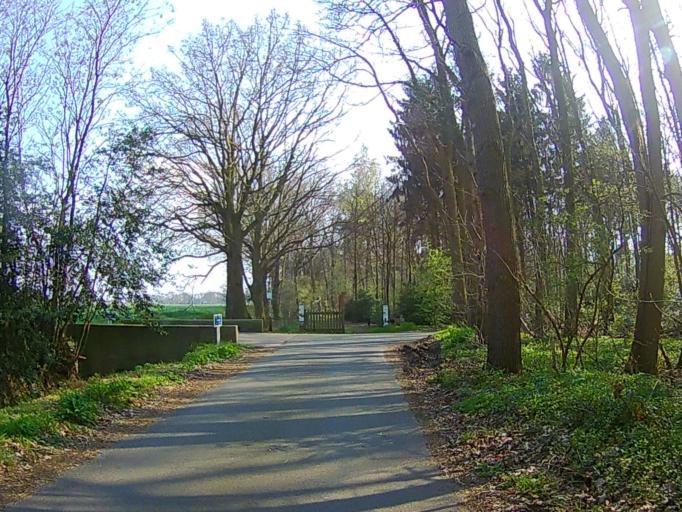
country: BE
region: Flanders
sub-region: Provincie Antwerpen
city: Essen
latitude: 51.4533
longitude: 4.5090
